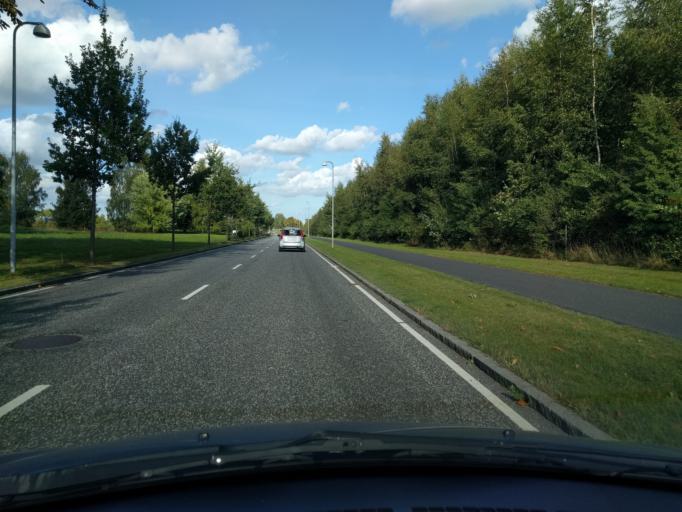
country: DK
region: South Denmark
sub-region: Odense Kommune
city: Neder Holluf
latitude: 55.3663
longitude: 10.5015
